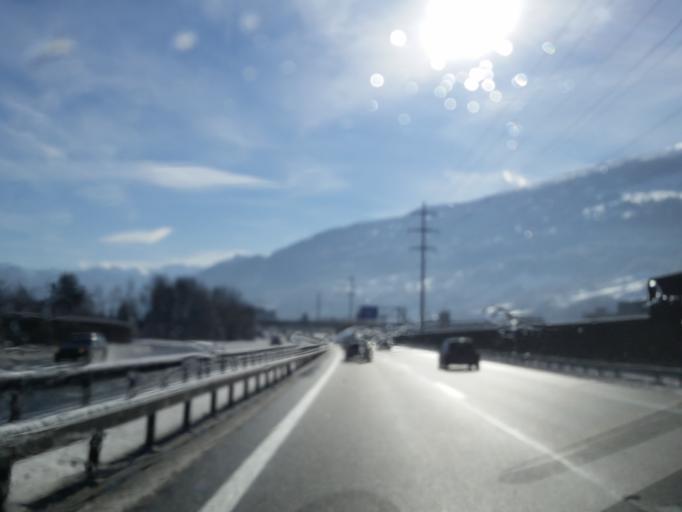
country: CH
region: Saint Gallen
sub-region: Wahlkreis Sarganserland
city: Sargans
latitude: 47.0458
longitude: 9.4327
